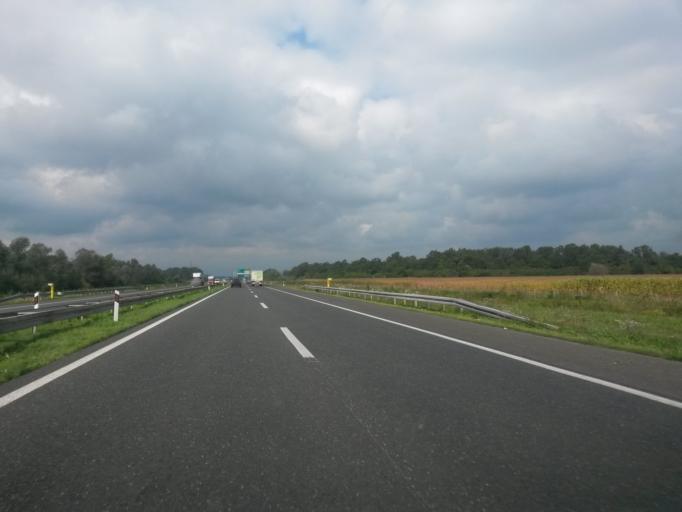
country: HR
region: Grad Zagreb
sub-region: Sesvete
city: Sesvete
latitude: 45.7798
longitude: 16.1929
